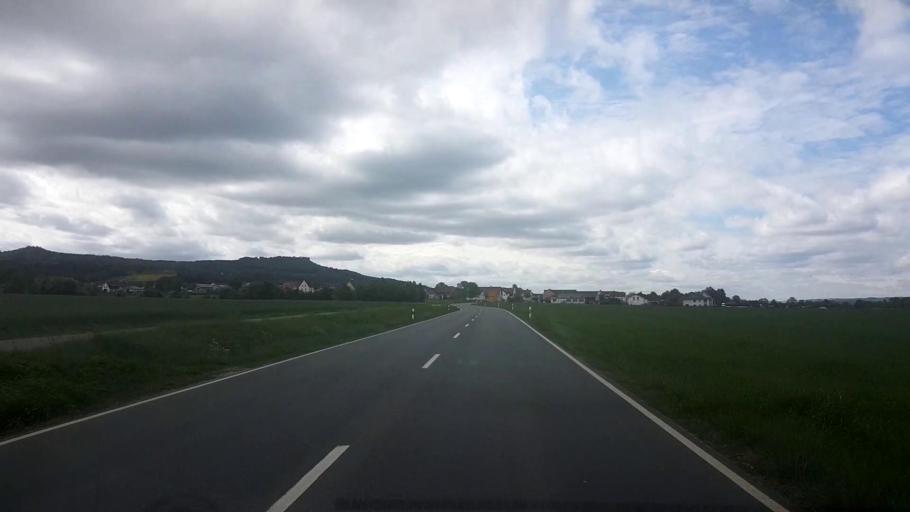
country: DE
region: Bavaria
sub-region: Upper Franconia
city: Lichtenfels
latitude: 50.1277
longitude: 11.0395
